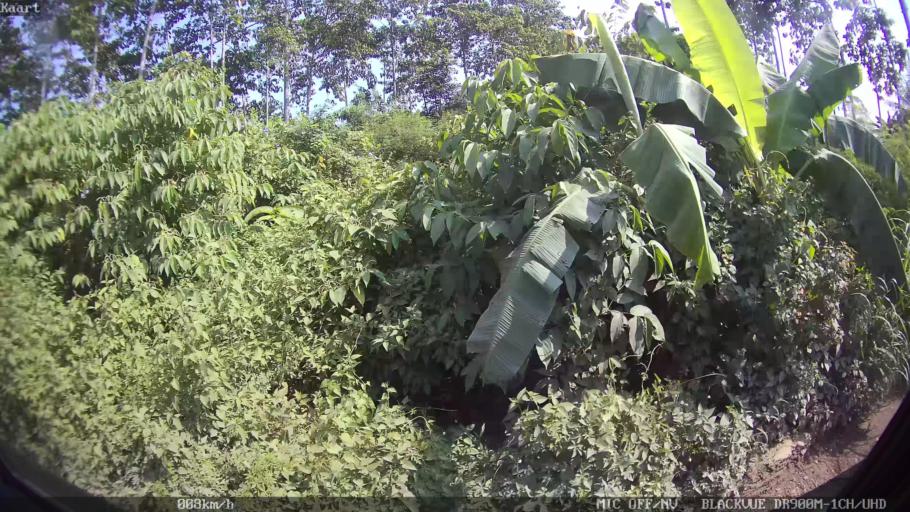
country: ID
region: Lampung
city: Natar
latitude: -5.2650
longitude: 105.2027
